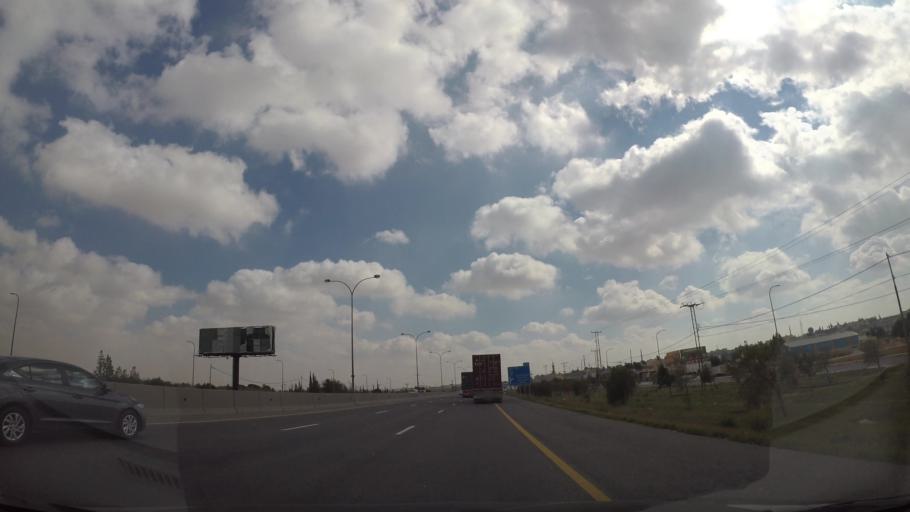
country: JO
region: Amman
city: Al Jizah
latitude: 31.7561
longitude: 35.9407
